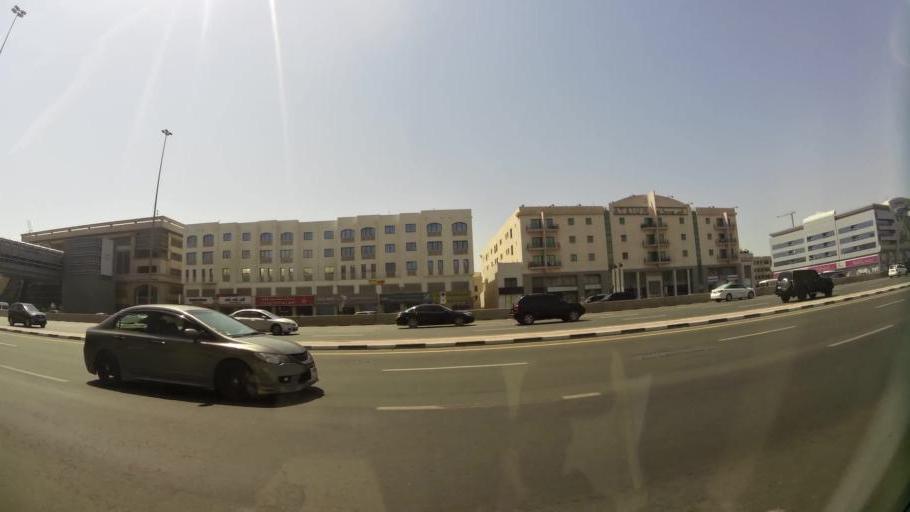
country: AE
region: Ash Shariqah
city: Sharjah
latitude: 25.2782
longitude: 55.3532
